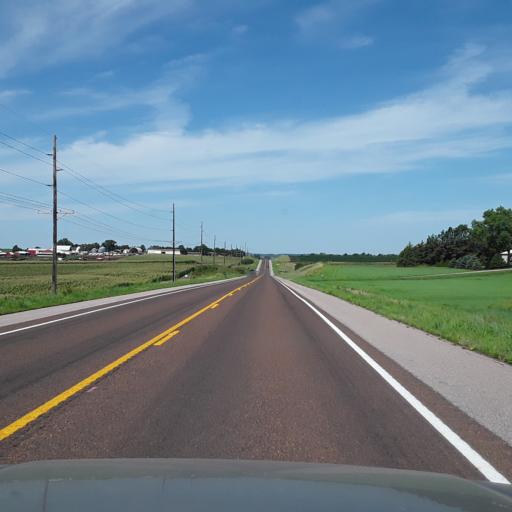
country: US
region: Nebraska
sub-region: Seward County
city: Milford
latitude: 40.8866
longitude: -96.8789
